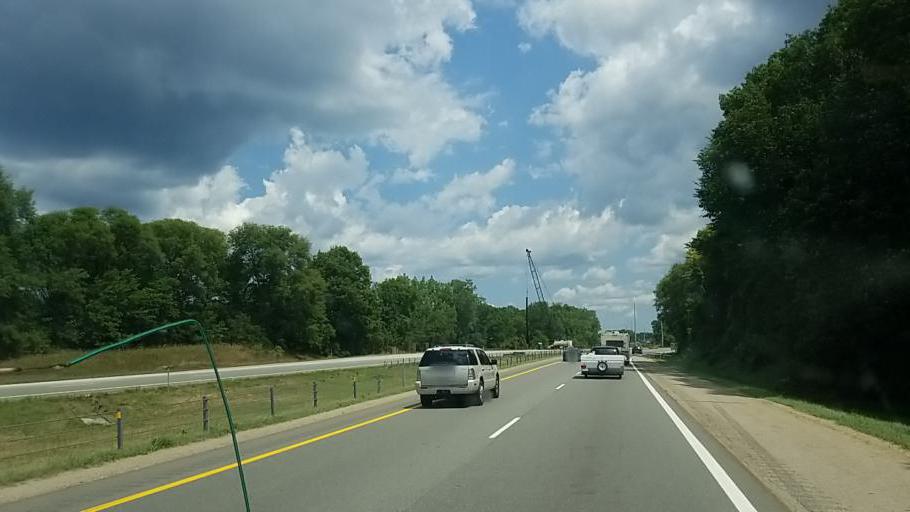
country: US
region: Michigan
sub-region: Kent County
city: Comstock Park
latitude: 43.0208
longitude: -85.6429
